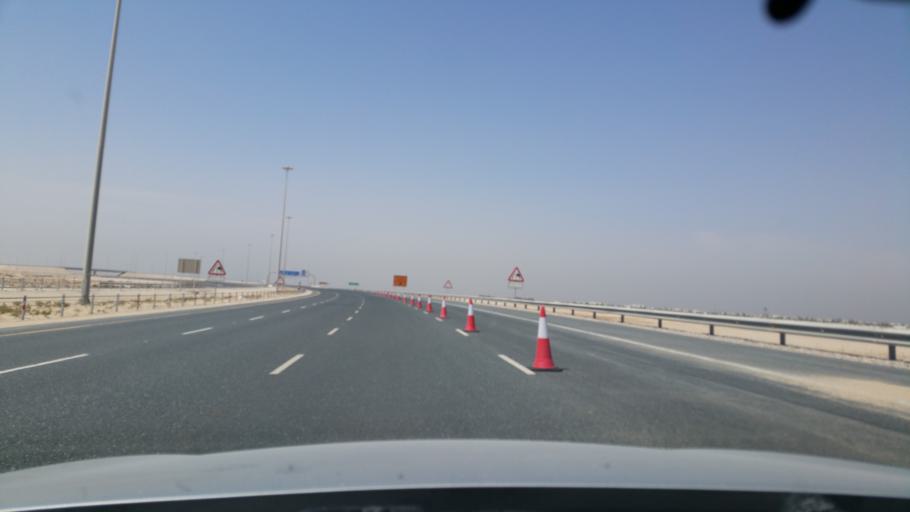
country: QA
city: Umm Bab
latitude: 24.8474
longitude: 50.8785
